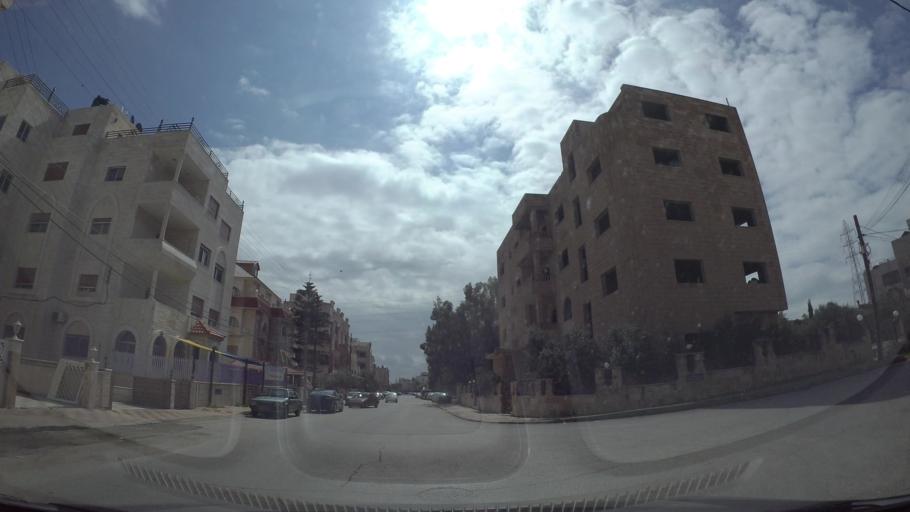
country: JO
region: Amman
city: Wadi as Sir
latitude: 31.9634
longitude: 35.8404
